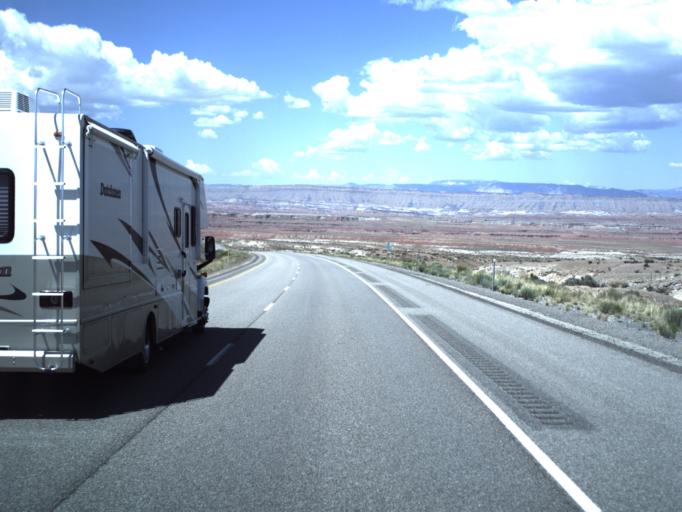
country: US
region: Utah
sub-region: Emery County
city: Ferron
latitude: 38.8461
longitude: -110.9903
